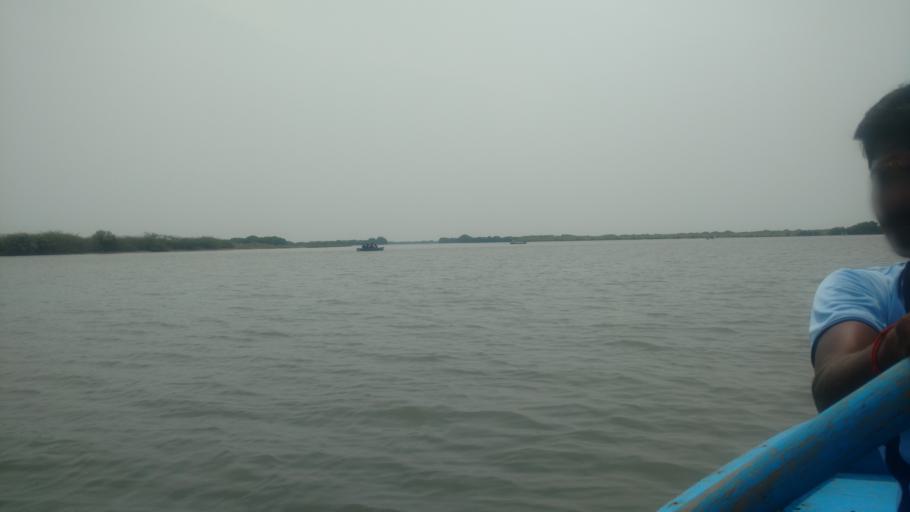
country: IN
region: Tamil Nadu
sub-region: Cuddalore
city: Annamalainagar
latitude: 11.4305
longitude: 79.7833
